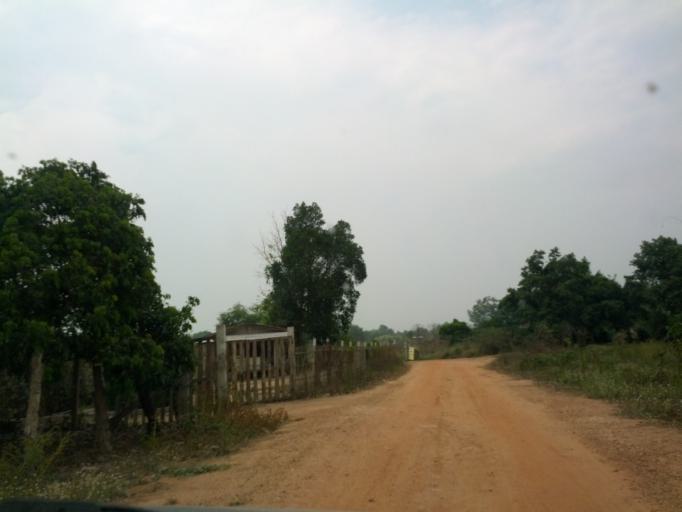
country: TH
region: Chiang Mai
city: Mae Taeng
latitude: 19.1179
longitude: 98.9960
